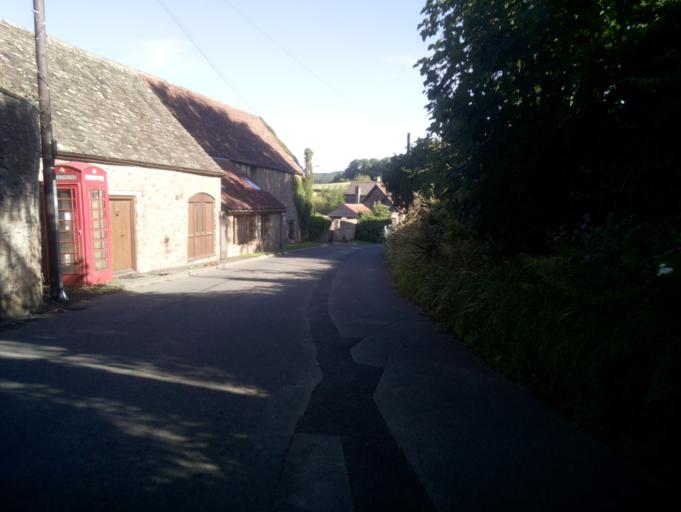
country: GB
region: England
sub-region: Gloucestershire
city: Coleford
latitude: 51.7837
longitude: -2.6491
